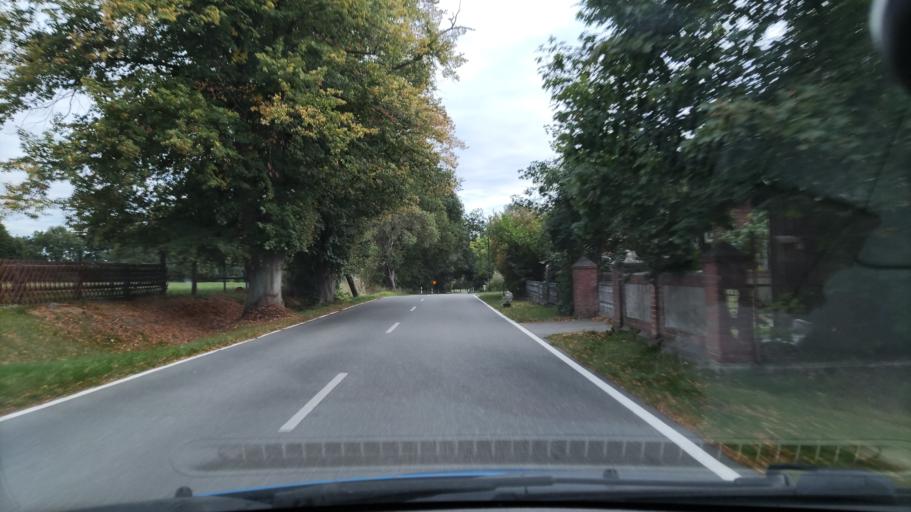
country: DE
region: Mecklenburg-Vorpommern
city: Boizenburg
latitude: 53.4255
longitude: 10.8407
